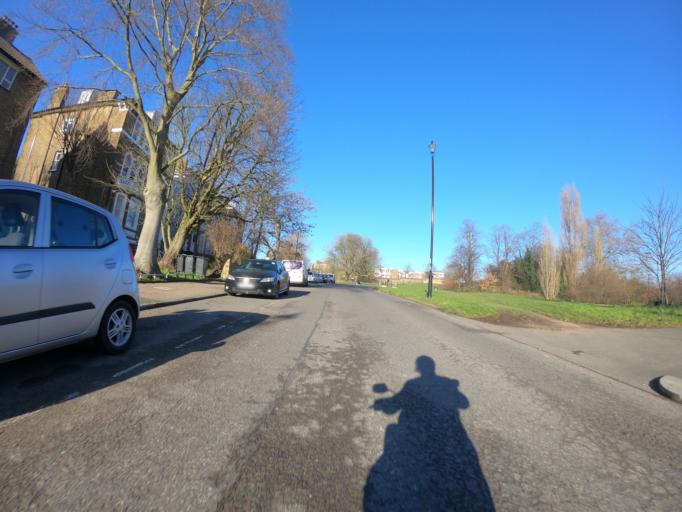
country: GB
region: England
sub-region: Greater London
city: Blackheath
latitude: 51.4684
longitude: -0.0087
